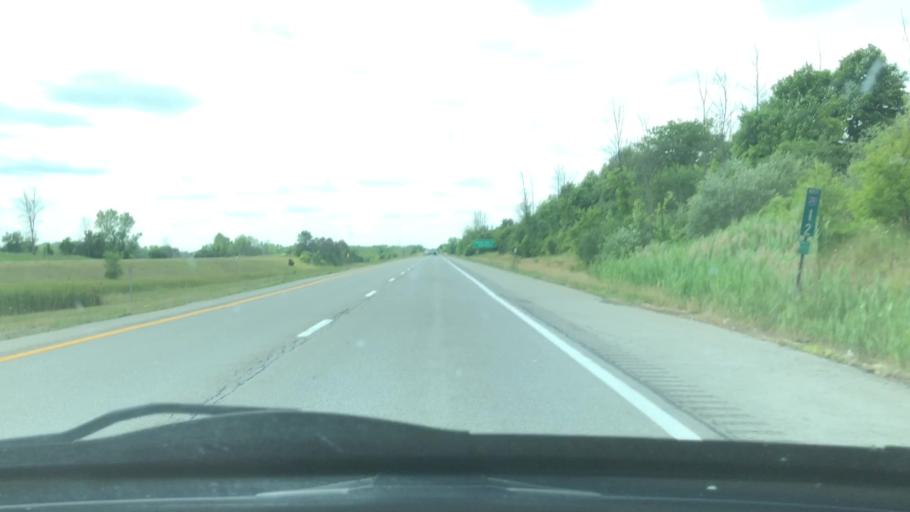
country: US
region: New York
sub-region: Monroe County
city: Spencerport
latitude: 43.1075
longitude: -77.7817
